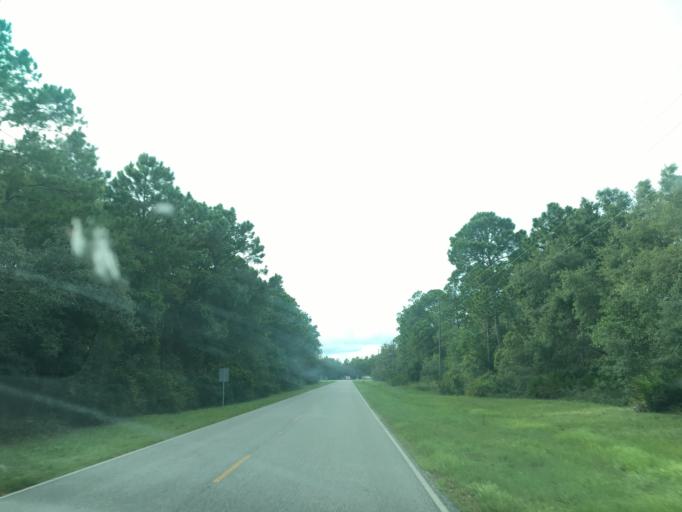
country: US
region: Florida
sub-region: Wakulla County
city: Crawfordville
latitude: 29.9409
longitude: -84.3844
